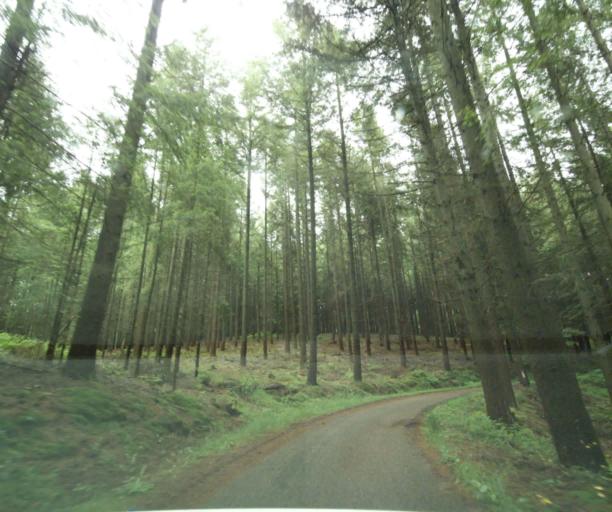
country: FR
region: Bourgogne
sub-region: Departement de Saone-et-Loire
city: Matour
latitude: 46.4487
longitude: 4.4675
